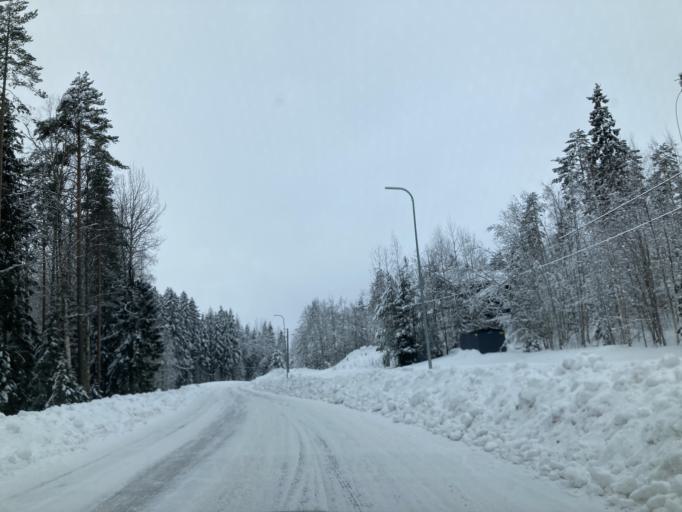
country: FI
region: Central Finland
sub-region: Jaemsae
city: Jaemsae
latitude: 61.8777
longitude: 25.3109
